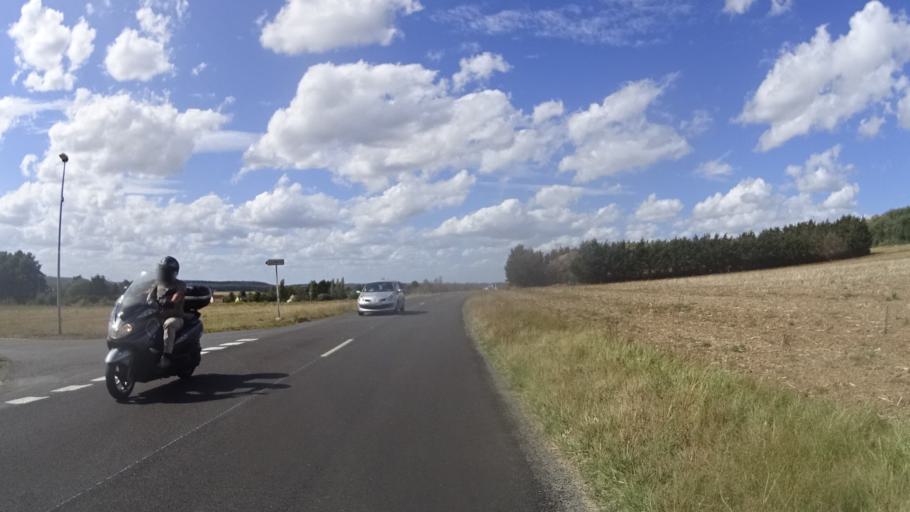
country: FR
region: Ile-de-France
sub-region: Departement de l'Essonne
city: La Ferte-Alais
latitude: 48.4580
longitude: 2.3556
